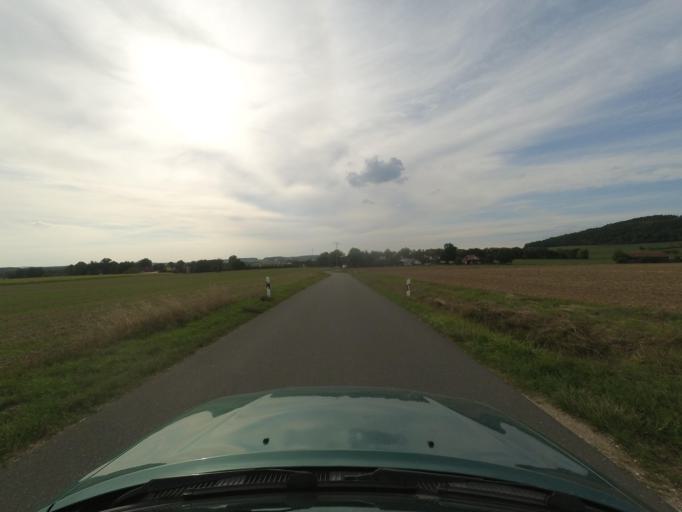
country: DE
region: Bavaria
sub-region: Upper Palatinate
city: Freystadt
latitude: 49.2204
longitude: 11.3316
